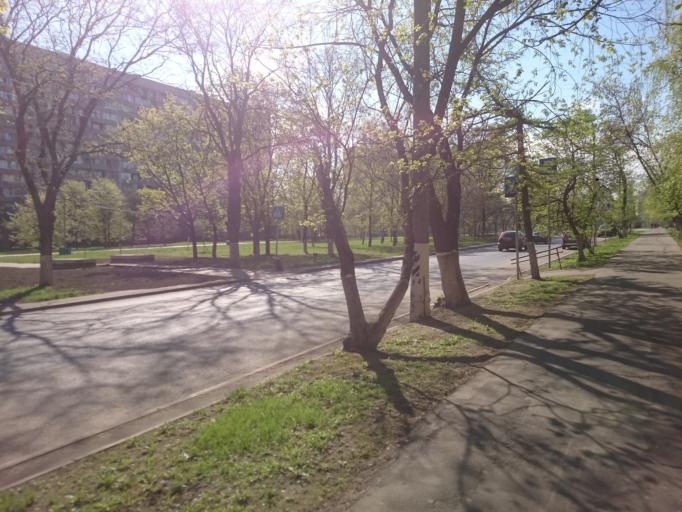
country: RU
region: Moscow
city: Tekstil'shchiki
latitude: 55.7137
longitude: 37.7436
